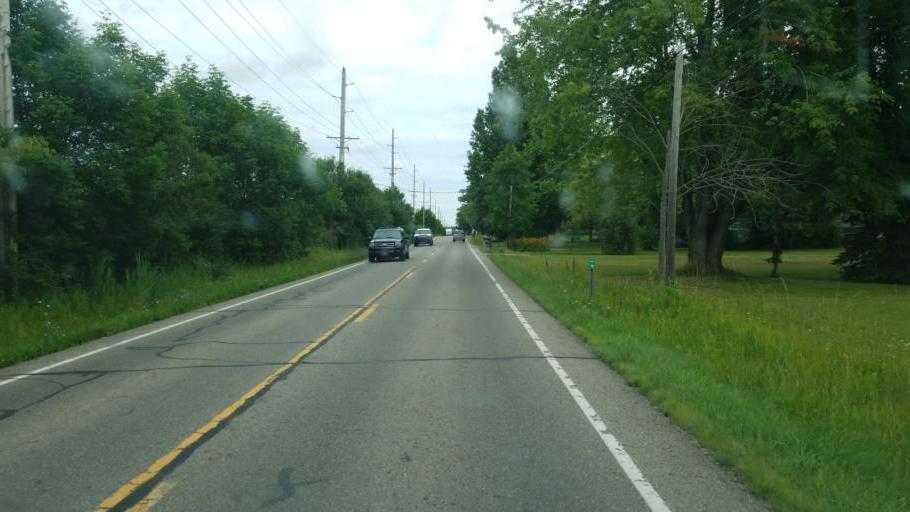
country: US
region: Ohio
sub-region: Geauga County
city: Burton
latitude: 41.4481
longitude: -81.2445
